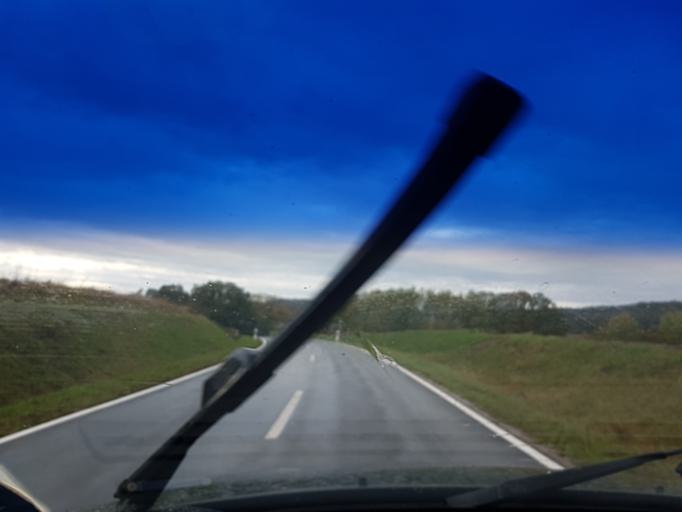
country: DE
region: Bavaria
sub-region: Upper Franconia
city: Schlusselfeld
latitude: 49.7629
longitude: 10.6641
